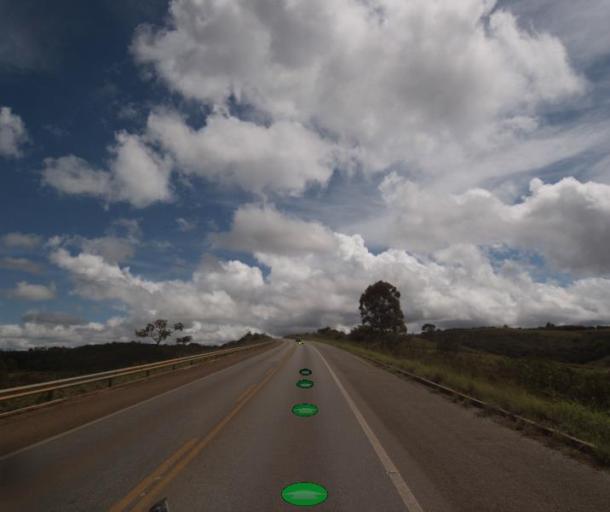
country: BR
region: Federal District
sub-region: Brasilia
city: Brasilia
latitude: -15.7427
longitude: -48.3734
